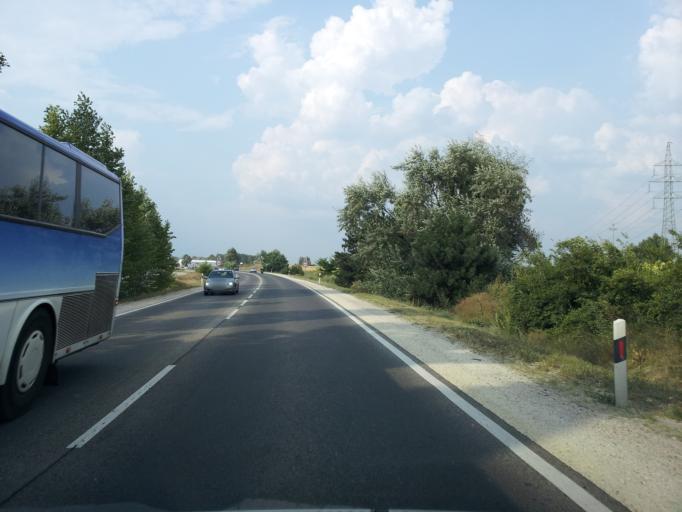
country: HU
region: Pest
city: Dunaharaszti
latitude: 47.3513
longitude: 19.1230
